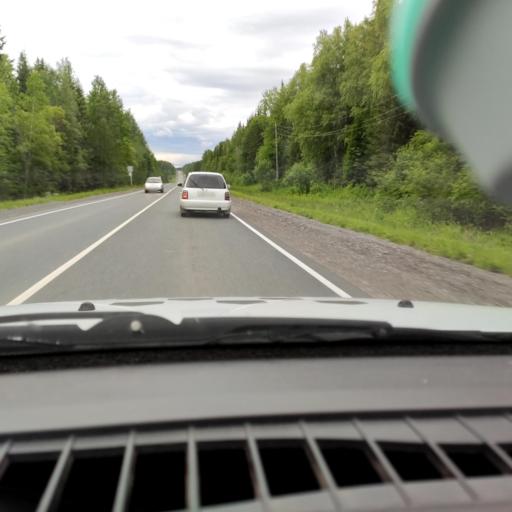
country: RU
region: Perm
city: Chusovoy
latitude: 58.2320
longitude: 57.8268
